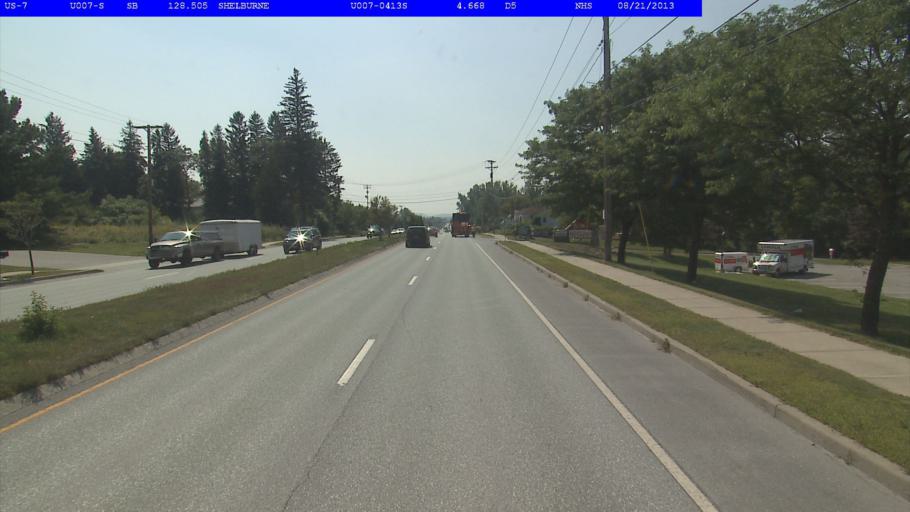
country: US
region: Vermont
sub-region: Chittenden County
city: Burlington
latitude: 44.4155
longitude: -73.2138
